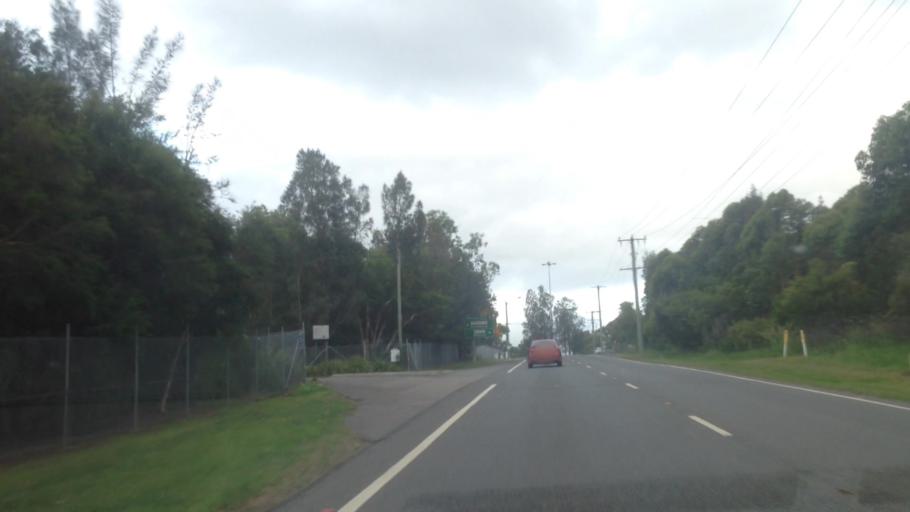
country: AU
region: New South Wales
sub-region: Lake Macquarie Shire
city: Dora Creek
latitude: -33.1137
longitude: 151.4757
